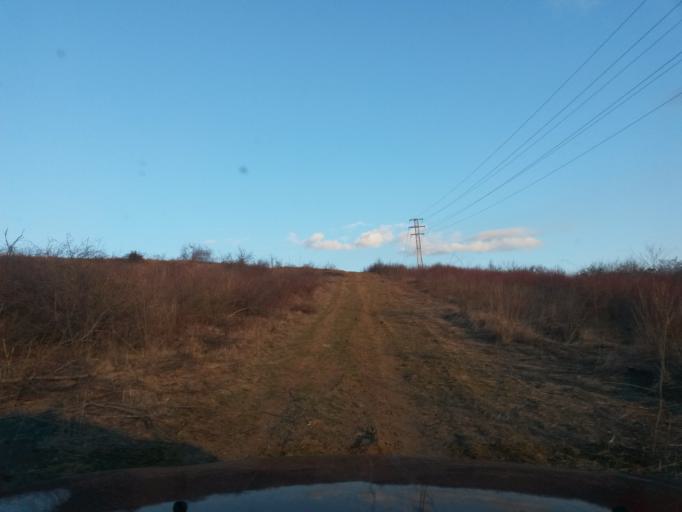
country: SK
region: Kosicky
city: Kosice
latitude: 48.6963
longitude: 21.3470
